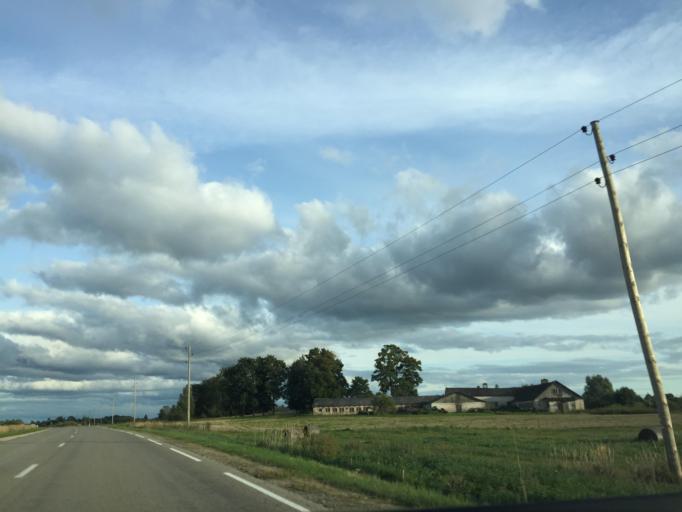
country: LV
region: Nereta
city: Nereta
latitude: 56.2631
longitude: 25.1822
